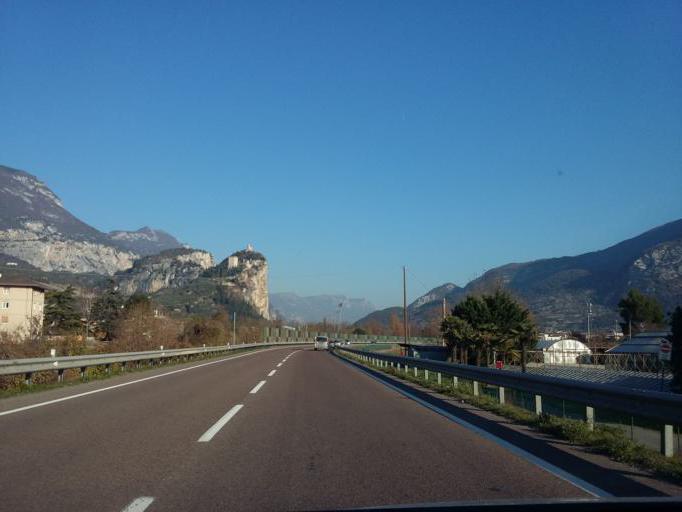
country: IT
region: Trentino-Alto Adige
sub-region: Provincia di Trento
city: Arco
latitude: 45.9106
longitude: 10.8843
